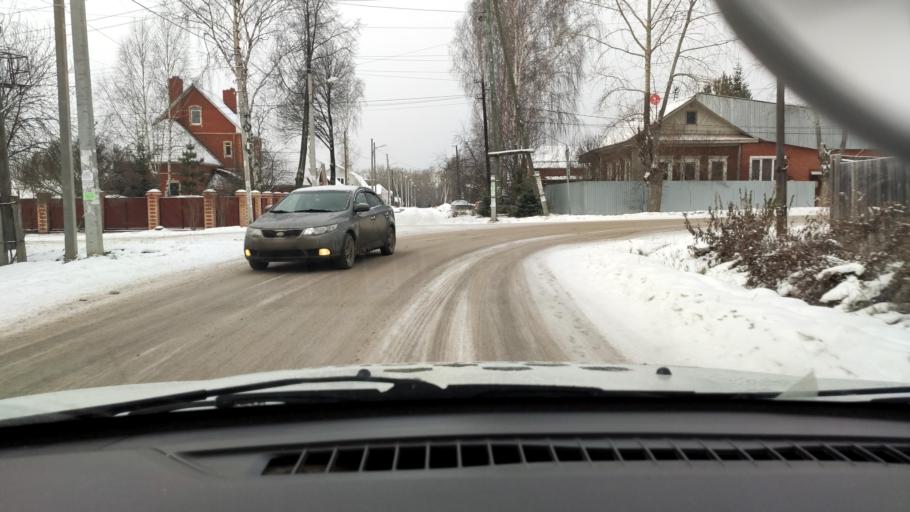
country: RU
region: Perm
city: Polazna
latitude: 58.1180
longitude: 56.3946
